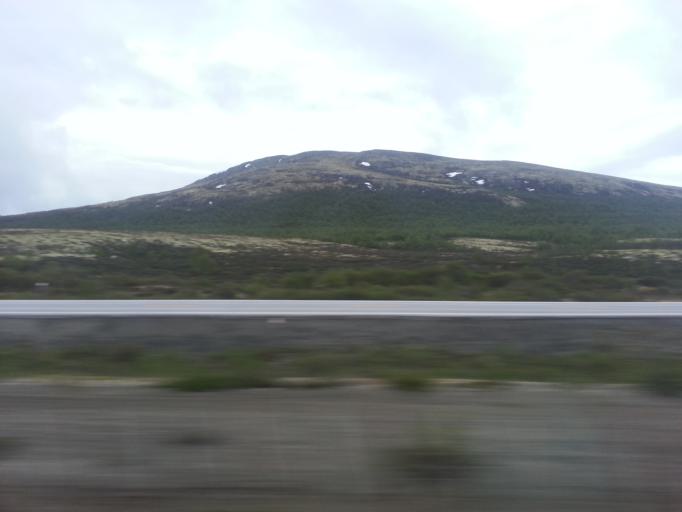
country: NO
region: Sor-Trondelag
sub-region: Oppdal
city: Oppdal
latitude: 62.2575
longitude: 9.5514
